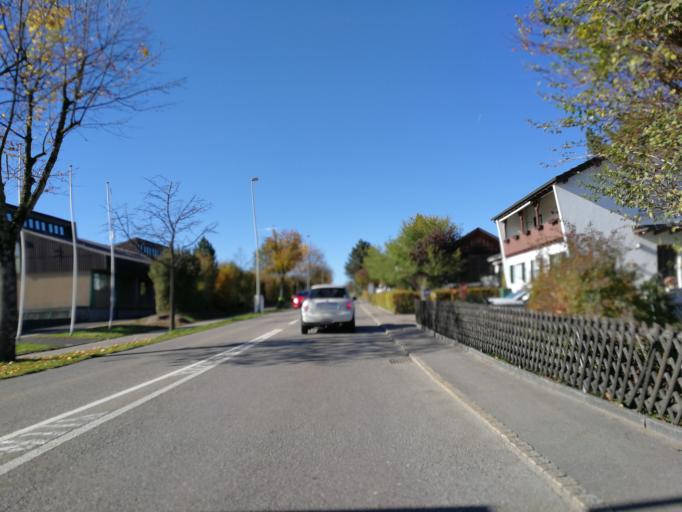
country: CH
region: Zurich
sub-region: Bezirk Hinwil
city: Binzikon
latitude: 47.2838
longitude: 8.7586
